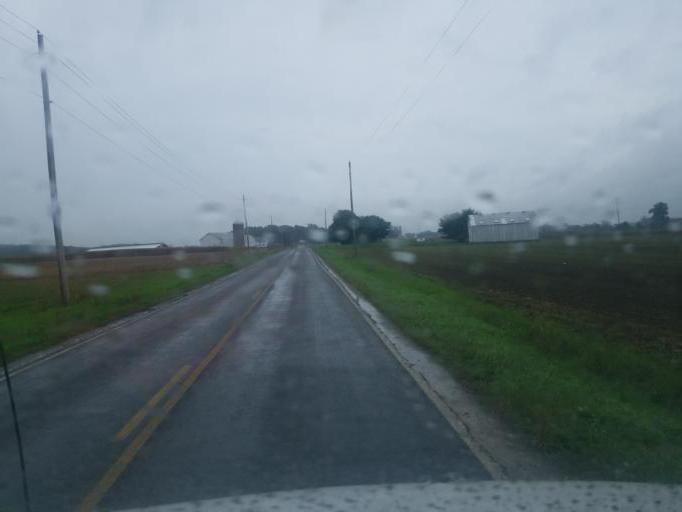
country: US
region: Ohio
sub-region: Medina County
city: Seville
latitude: 41.0009
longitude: -81.8584
